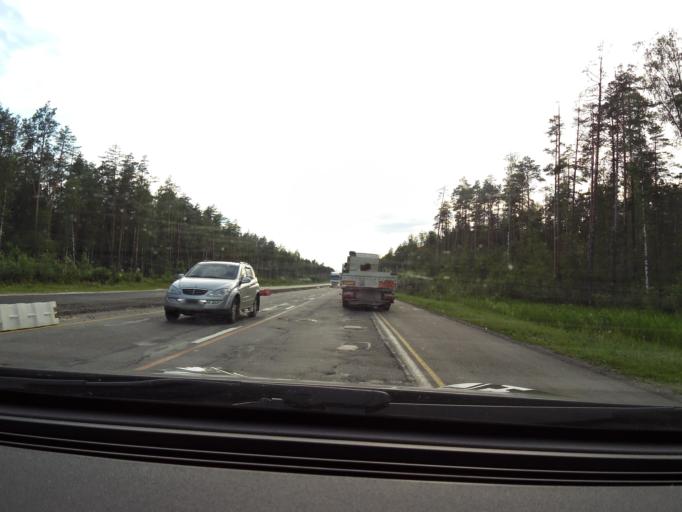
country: RU
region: Vladimir
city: Orgtrud
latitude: 56.1028
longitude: 40.7333
